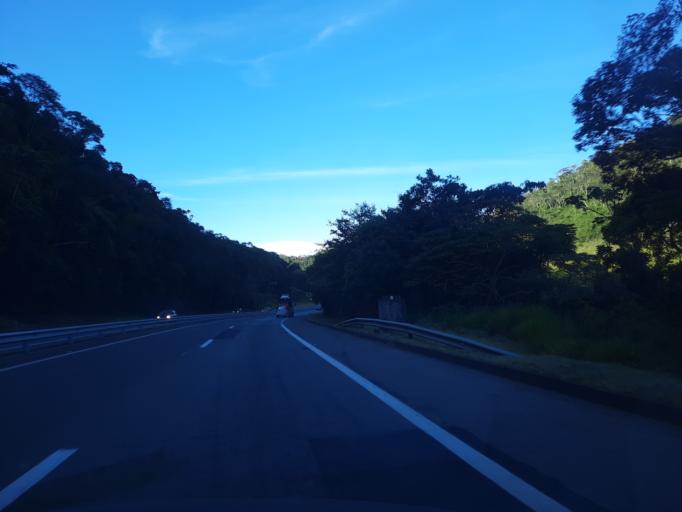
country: BR
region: Rio de Janeiro
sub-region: Petropolis
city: Petropolis
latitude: -22.4174
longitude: -43.1526
